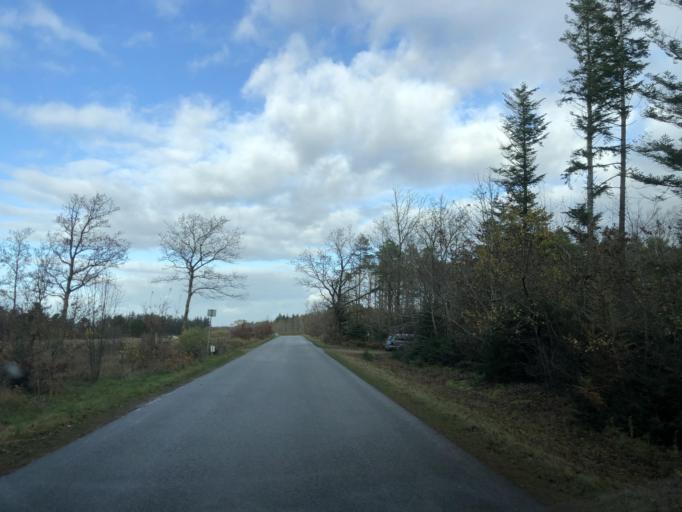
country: DK
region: Central Jutland
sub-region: Holstebro Kommune
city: Ulfborg
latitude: 56.1796
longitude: 8.4202
